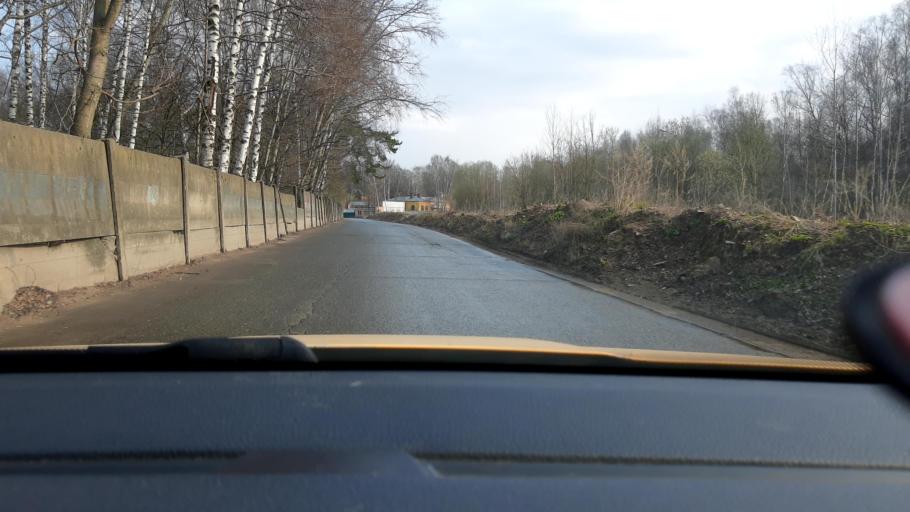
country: RU
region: Moscow
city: Babushkin
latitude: 55.8519
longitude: 37.7015
